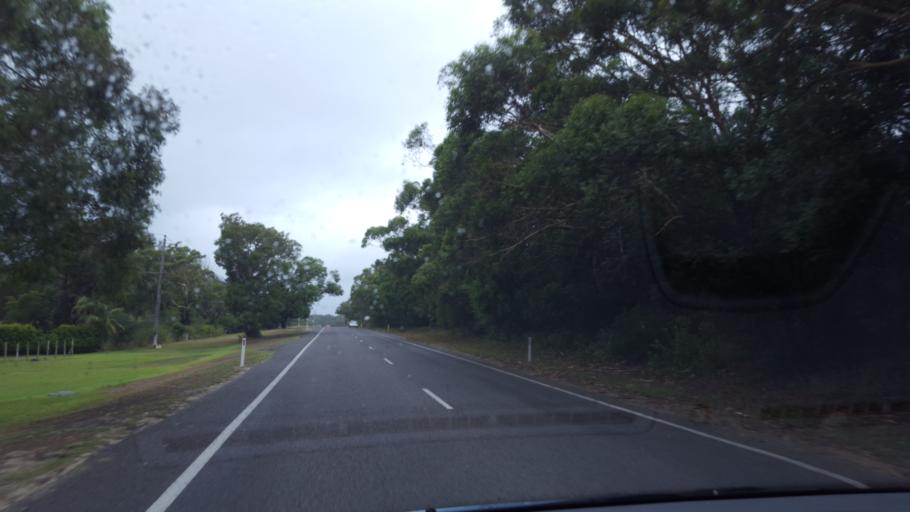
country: AU
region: New South Wales
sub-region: Port Stephens Shire
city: Anna Bay
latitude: -32.7727
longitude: 152.0769
